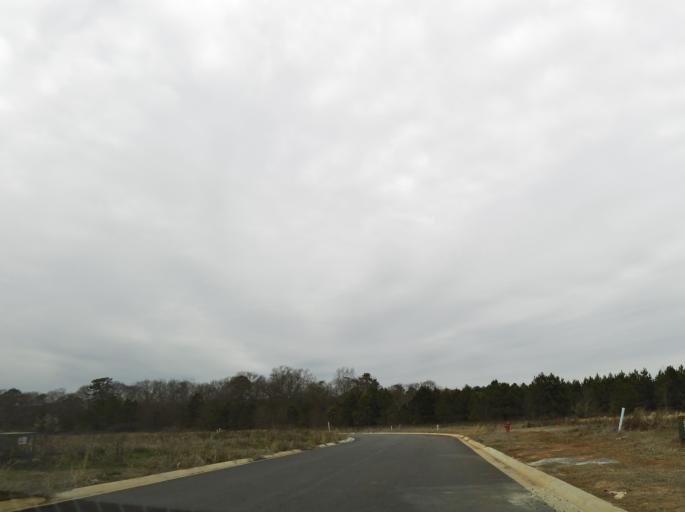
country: US
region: Georgia
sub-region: Peach County
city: Byron
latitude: 32.6108
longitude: -83.7595
